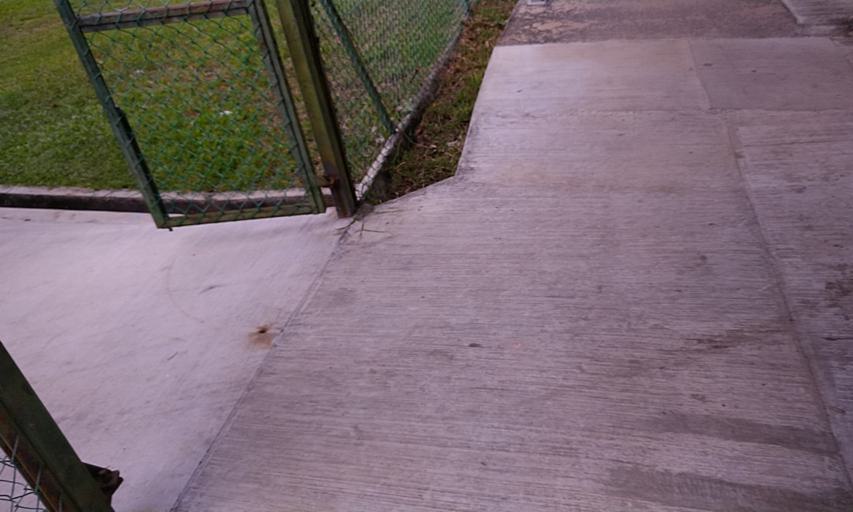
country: SG
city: Singapore
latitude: 1.2869
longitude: 103.8138
